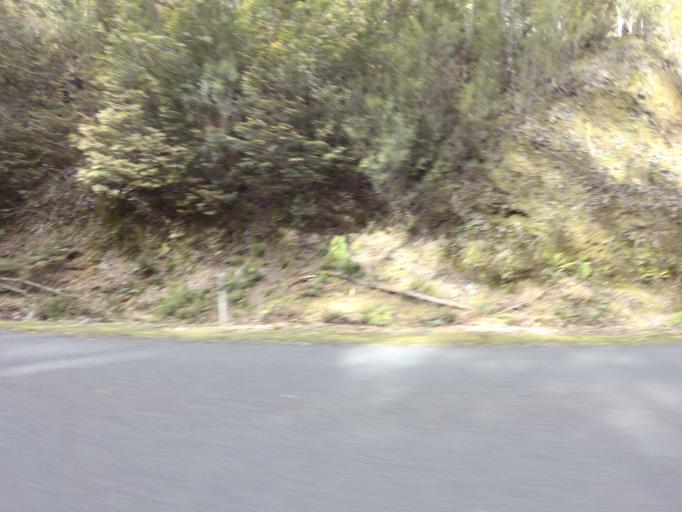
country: AU
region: Tasmania
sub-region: Huon Valley
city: Geeveston
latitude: -42.8205
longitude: 146.2939
